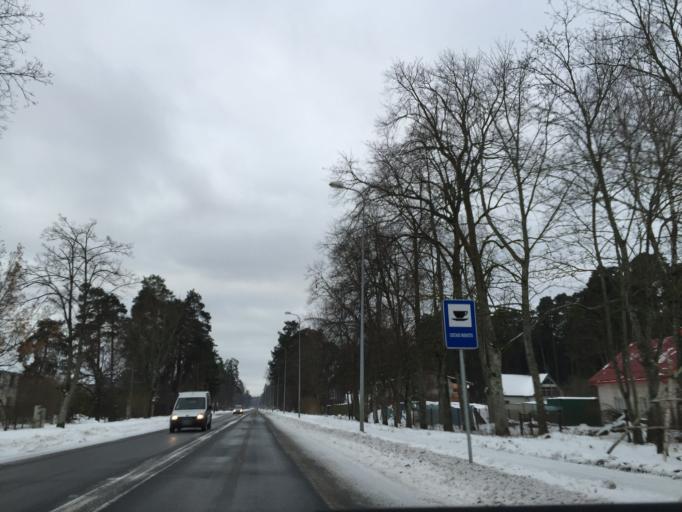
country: LV
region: Saulkrastu
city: Saulkrasti
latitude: 57.2465
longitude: 24.4052
